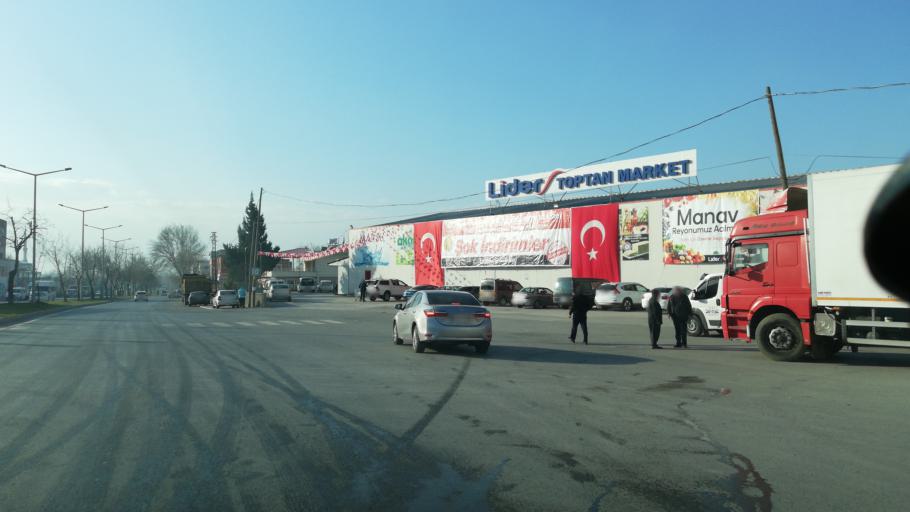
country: TR
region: Kahramanmaras
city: Kahramanmaras
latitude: 37.5655
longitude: 36.9167
